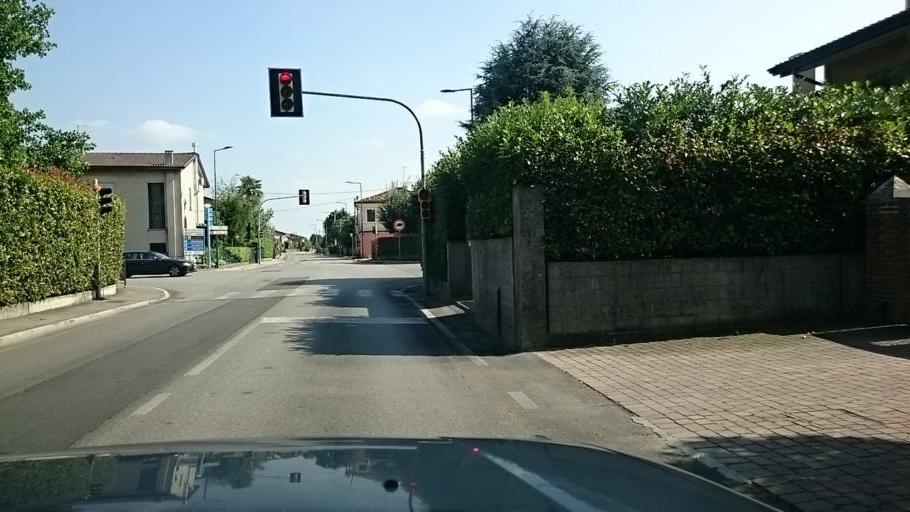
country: IT
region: Veneto
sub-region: Provincia di Padova
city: San Martino di Lupari
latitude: 45.6445
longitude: 11.8503
